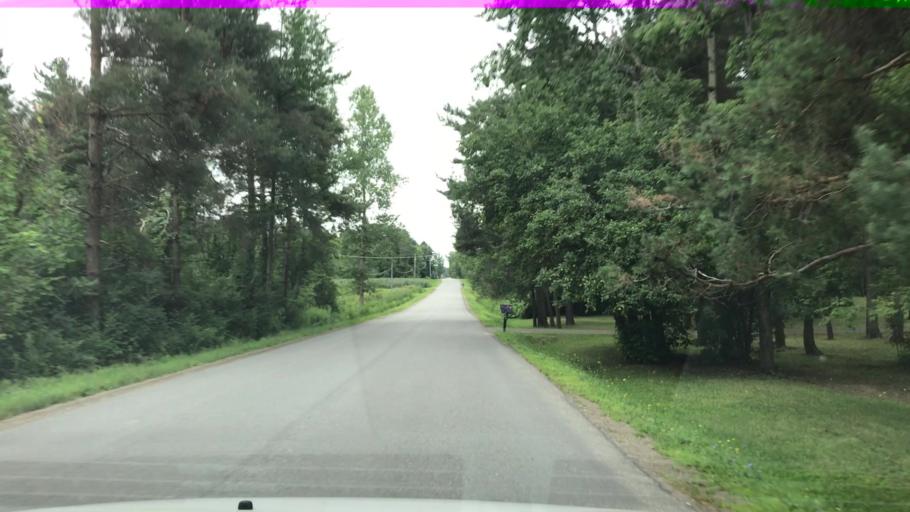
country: US
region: New York
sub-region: Wyoming County
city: Attica
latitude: 42.8357
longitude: -78.3365
